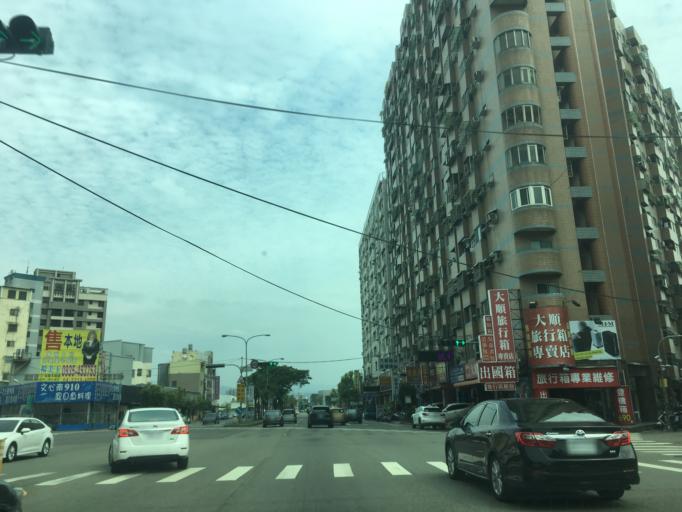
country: TW
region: Taiwan
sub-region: Taichung City
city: Taichung
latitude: 24.1112
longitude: 120.6594
